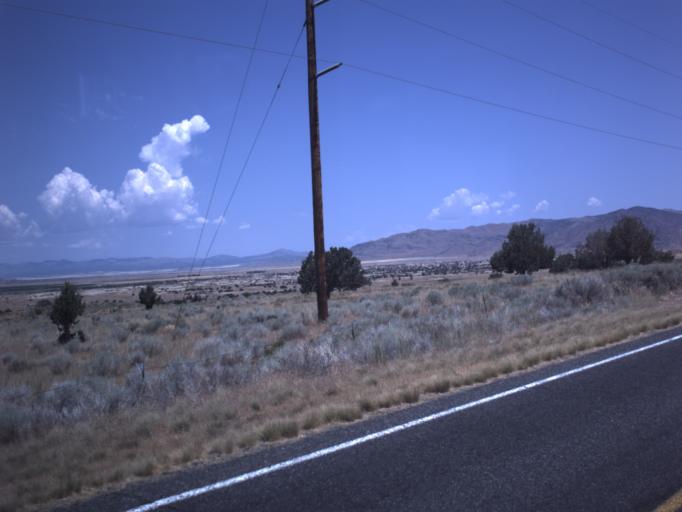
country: US
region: Utah
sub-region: Millard County
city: Delta
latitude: 39.4522
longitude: -112.3053
